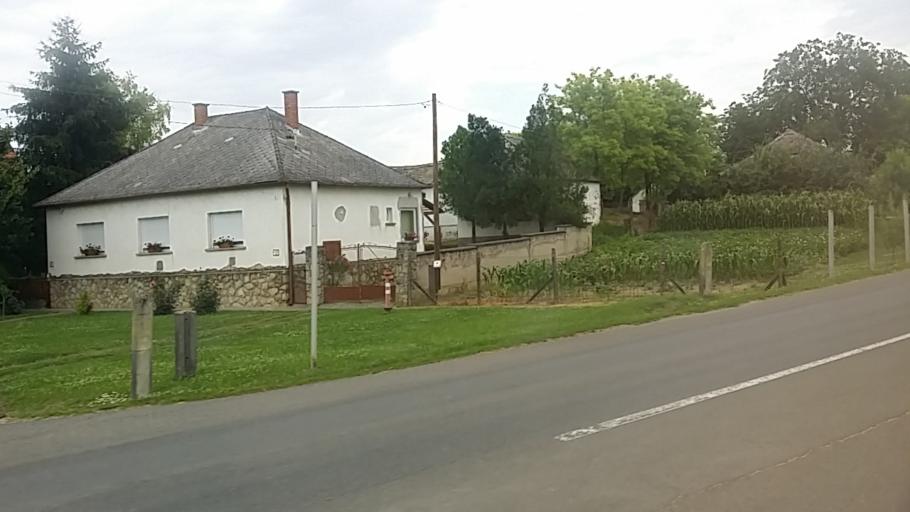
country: HU
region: Baranya
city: Boly
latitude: 45.9868
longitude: 18.5386
